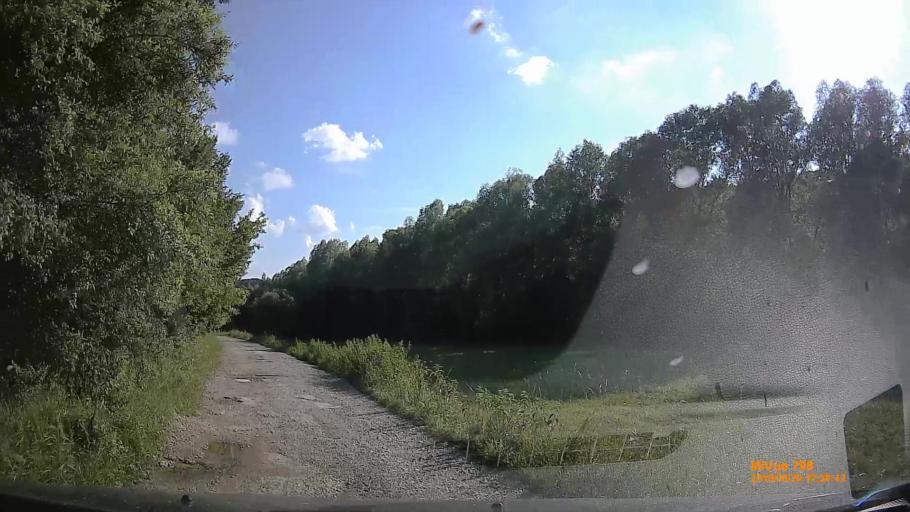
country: HU
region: Baranya
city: Buekkoesd
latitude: 46.1405
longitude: 18.0067
